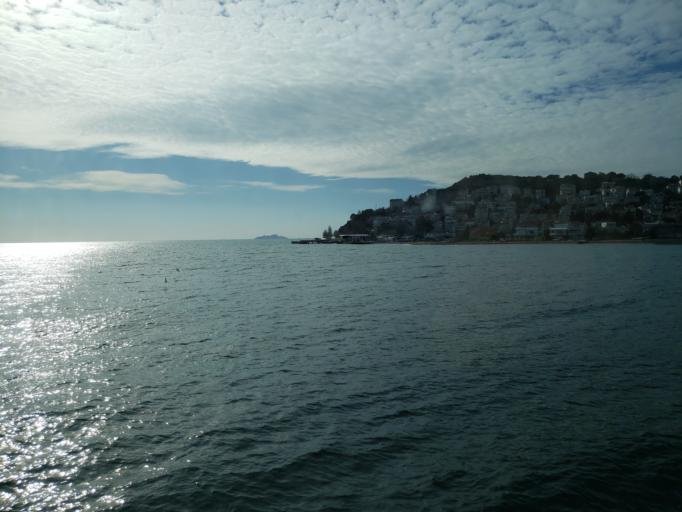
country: TR
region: Istanbul
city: Kinali
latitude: 40.9065
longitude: 29.0599
